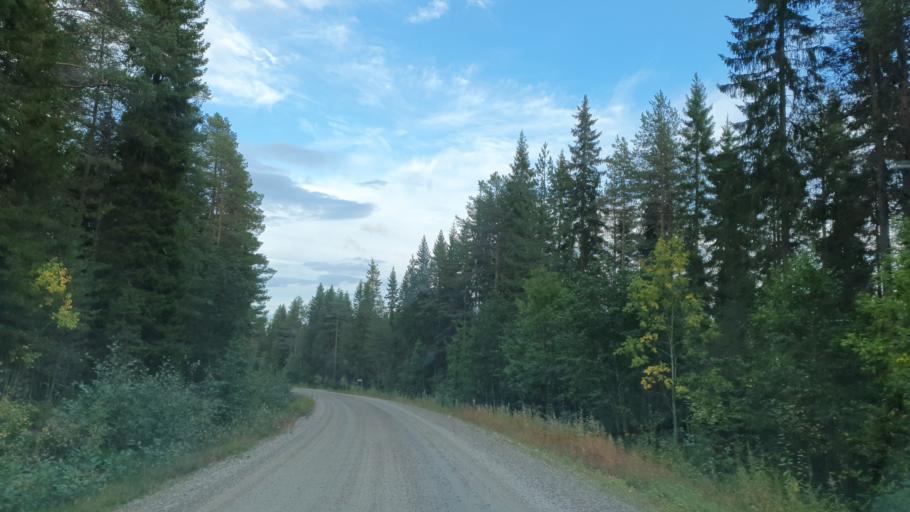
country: FI
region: Kainuu
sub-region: Kehys-Kainuu
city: Kuhmo
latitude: 64.3556
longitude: 29.5753
